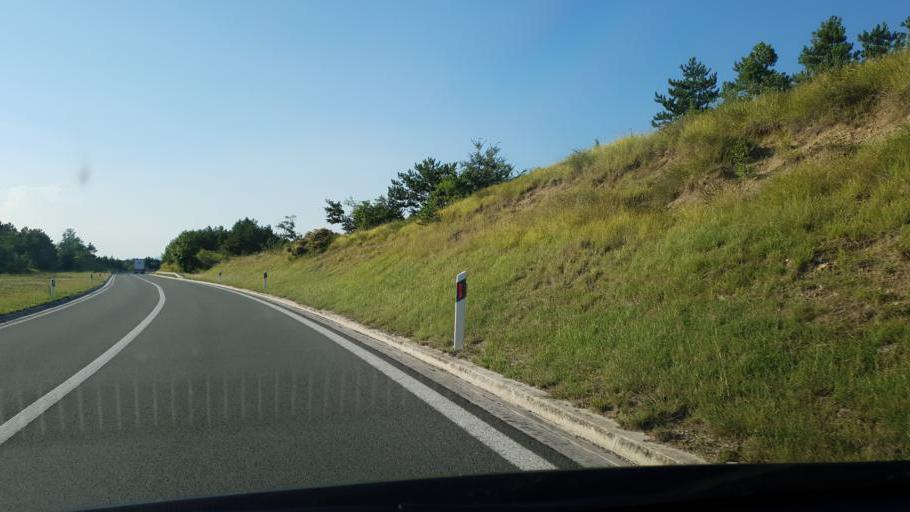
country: HR
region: Istarska
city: Buzet
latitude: 45.3260
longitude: 14.0757
